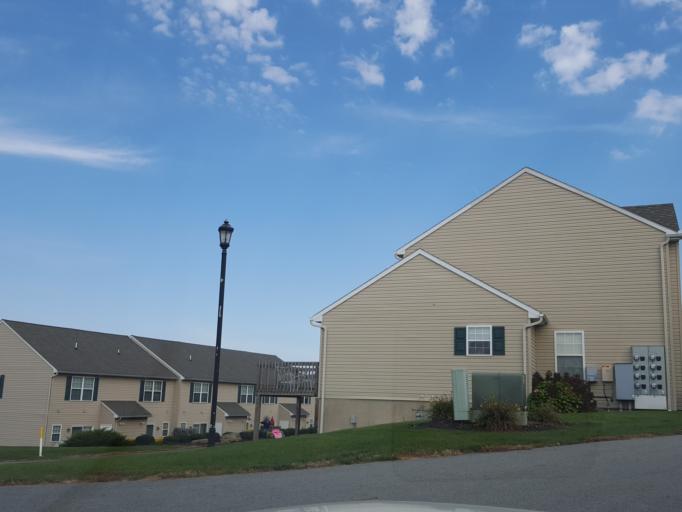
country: US
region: Pennsylvania
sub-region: York County
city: Yoe
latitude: 39.9195
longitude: -76.6272
